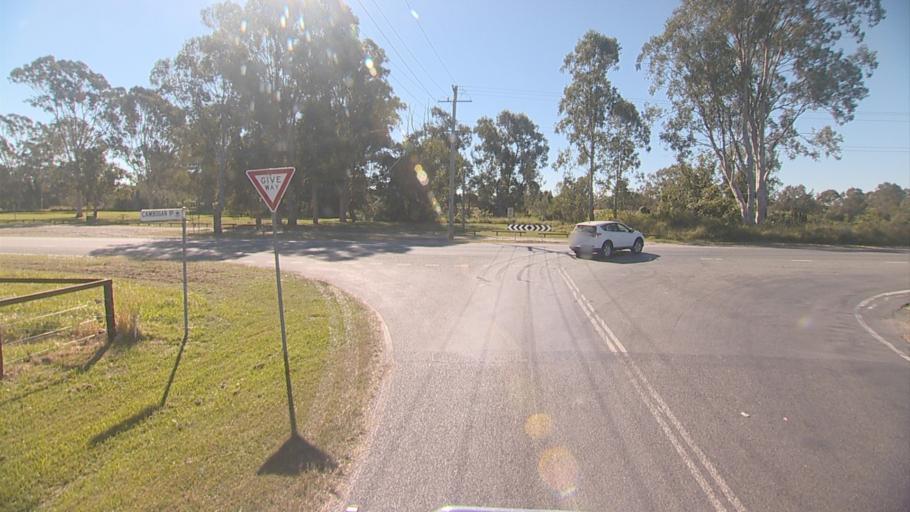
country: AU
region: Queensland
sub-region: Logan
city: Waterford West
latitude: -27.7093
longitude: 153.1409
